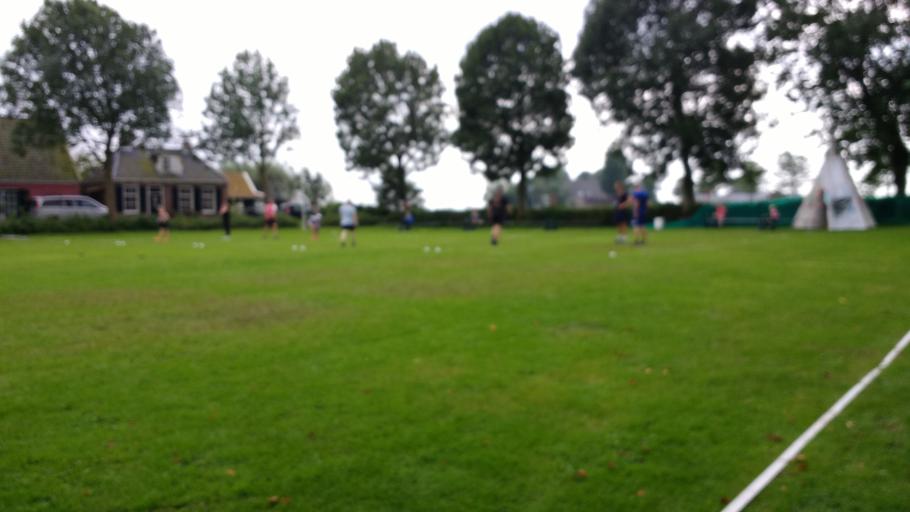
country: NL
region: Friesland
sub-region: Gemeente Littenseradiel
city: Winsum
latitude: 53.1597
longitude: 5.6671
